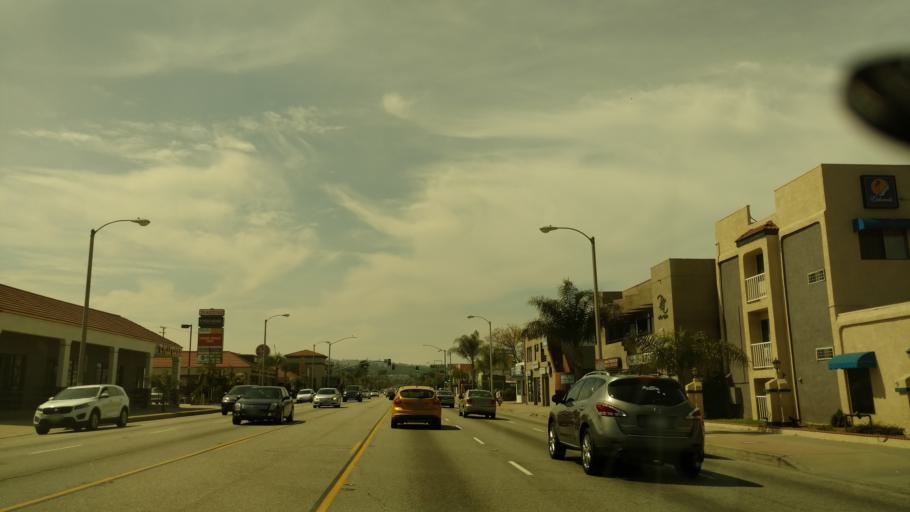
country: US
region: California
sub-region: Los Angeles County
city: Lomita
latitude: 33.7895
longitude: -118.3155
